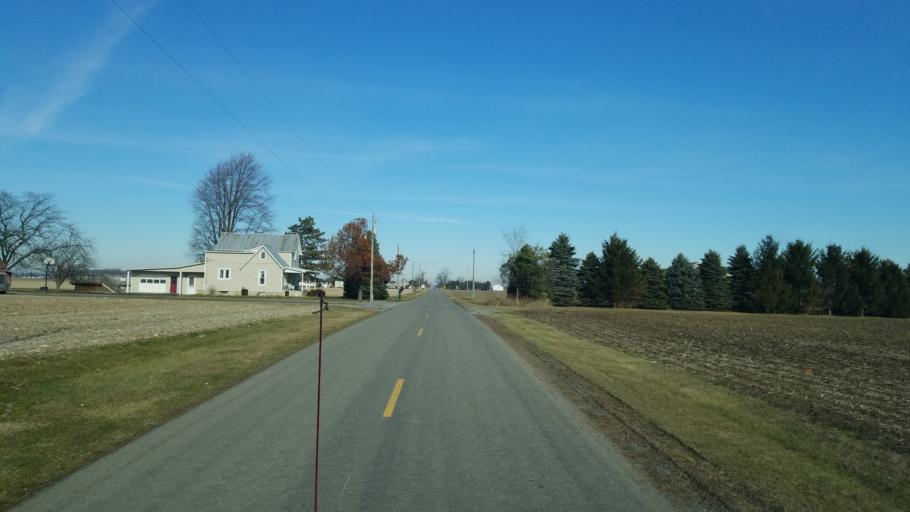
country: US
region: Ohio
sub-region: Putnam County
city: Pandora
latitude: 40.9228
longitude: -83.9379
